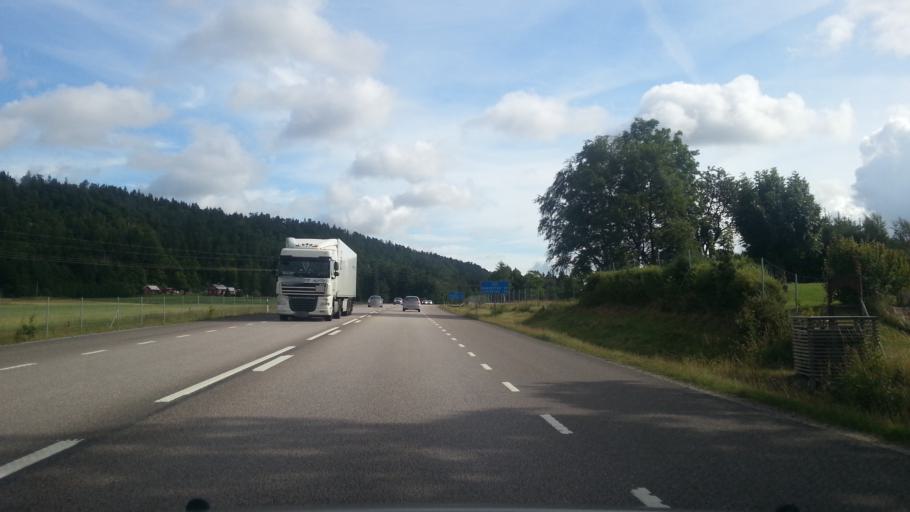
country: SE
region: Vaestra Goetaland
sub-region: Vanersborgs Kommun
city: Vargon
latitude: 58.2965
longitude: 12.5056
